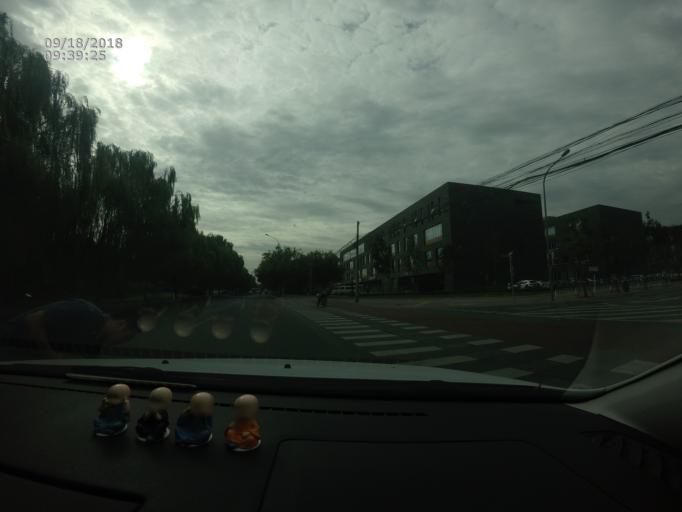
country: CN
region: Beijing
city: Xibeiwang
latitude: 40.0688
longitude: 116.2391
